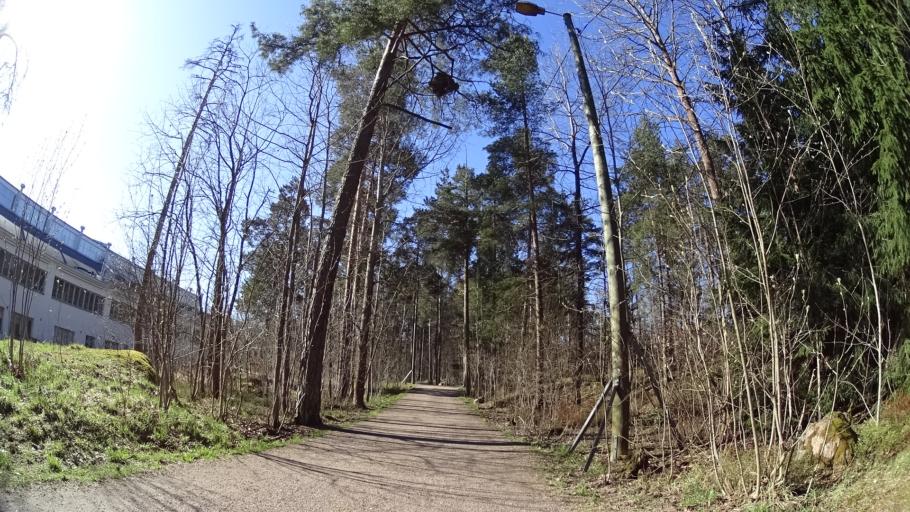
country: FI
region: Uusimaa
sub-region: Helsinki
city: Helsinki
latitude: 60.1993
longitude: 24.9095
